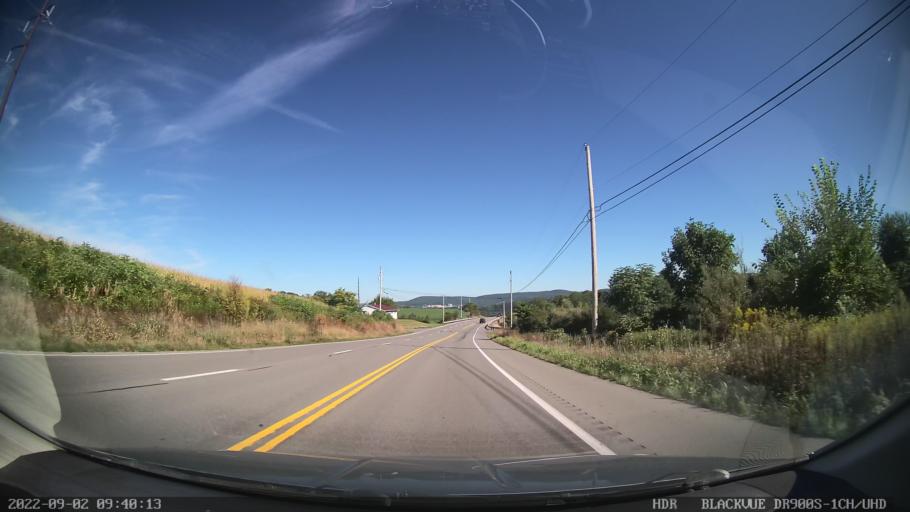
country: US
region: Pennsylvania
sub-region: Montour County
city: Mechanicsville
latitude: 40.9230
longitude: -76.5876
